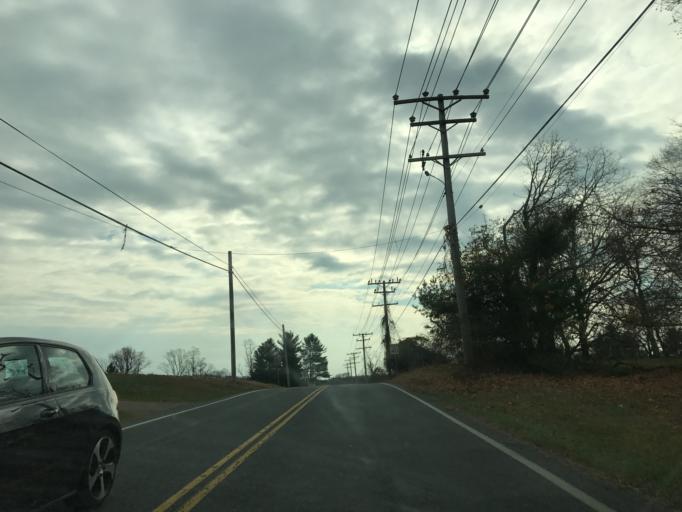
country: US
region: Maryland
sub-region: Harford County
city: Jarrettsville
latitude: 39.5858
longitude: -76.4293
